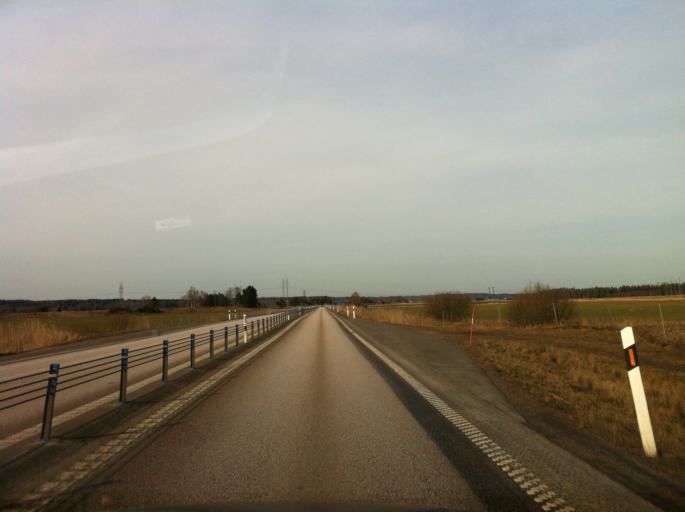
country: SE
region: Vaestra Goetaland
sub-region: Skovde Kommun
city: Stopen
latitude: 58.5572
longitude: 13.8055
